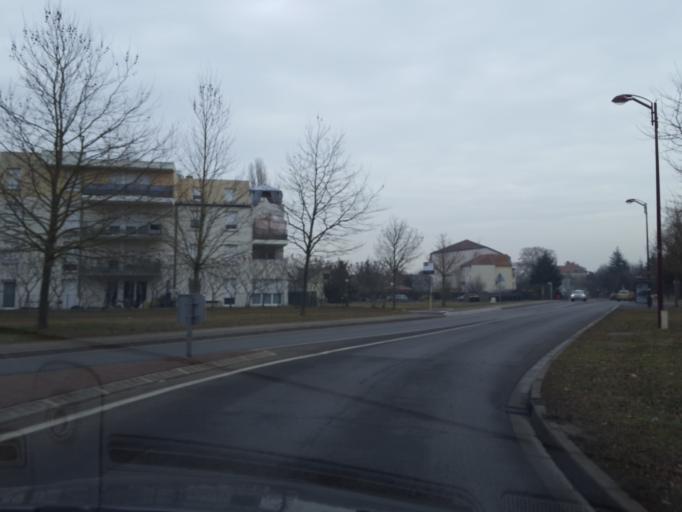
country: FR
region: Lorraine
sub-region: Departement de la Moselle
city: Moulins-les-Metz
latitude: 49.0906
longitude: 6.1223
